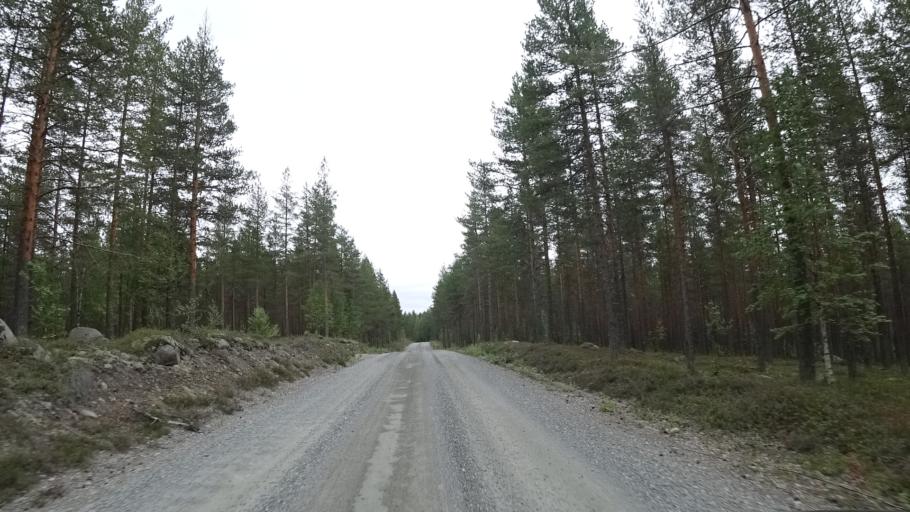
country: FI
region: North Karelia
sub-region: Pielisen Karjala
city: Lieksa
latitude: 63.3716
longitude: 30.3767
